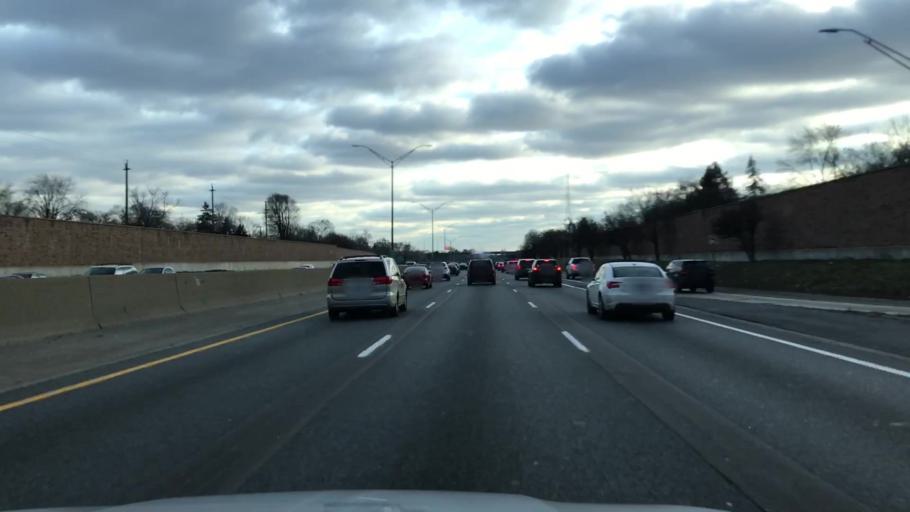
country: US
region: Michigan
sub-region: Oakland County
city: Madison Heights
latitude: 42.4872
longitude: -83.1153
